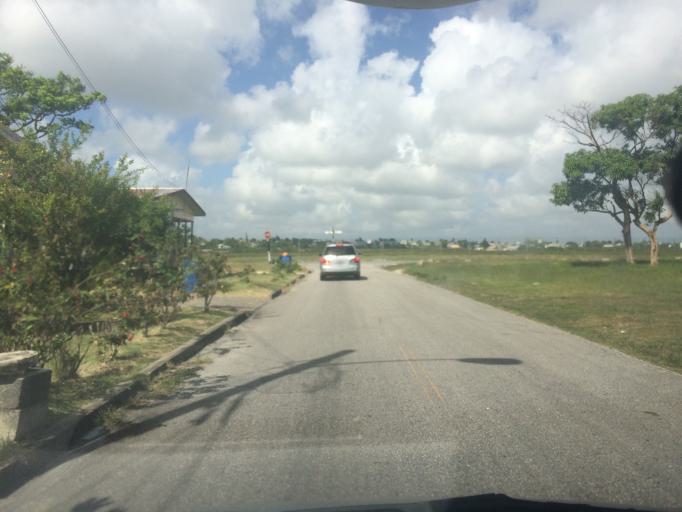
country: BB
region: Christ Church
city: Oistins
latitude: 13.0689
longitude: -59.5081
